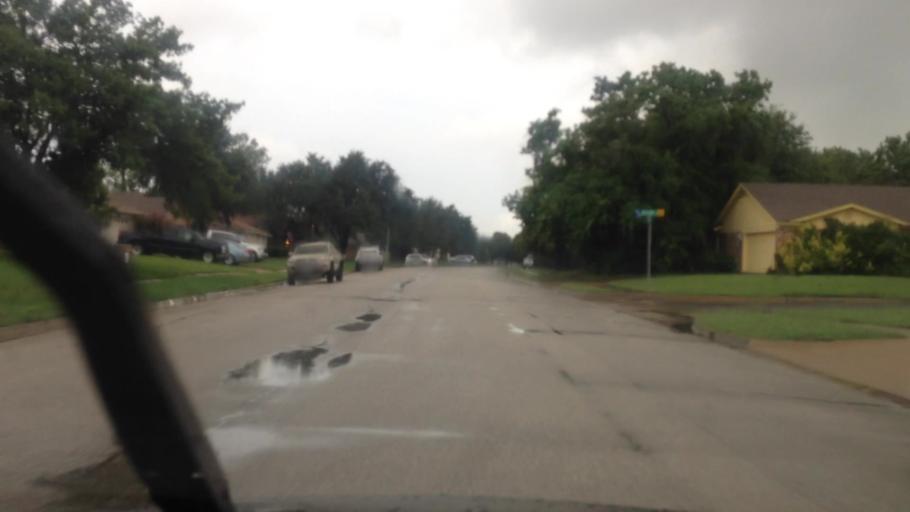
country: US
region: Texas
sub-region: Tarrant County
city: Colleyville
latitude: 32.8825
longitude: -97.2014
